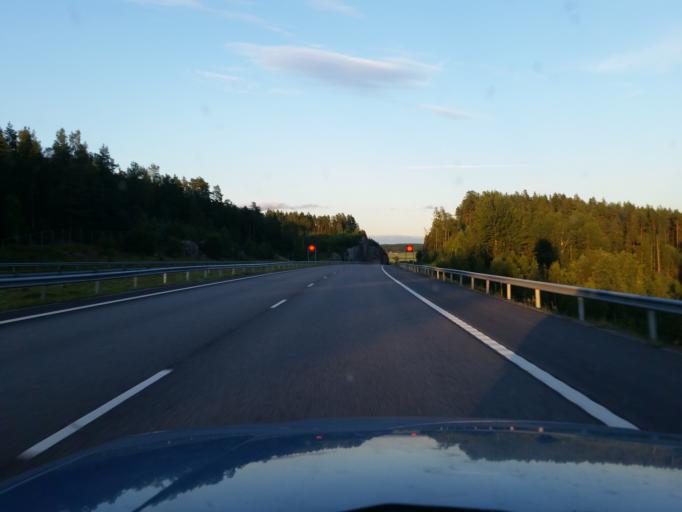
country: FI
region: Varsinais-Suomi
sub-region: Salo
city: Halikko
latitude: 60.4337
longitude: 22.9834
